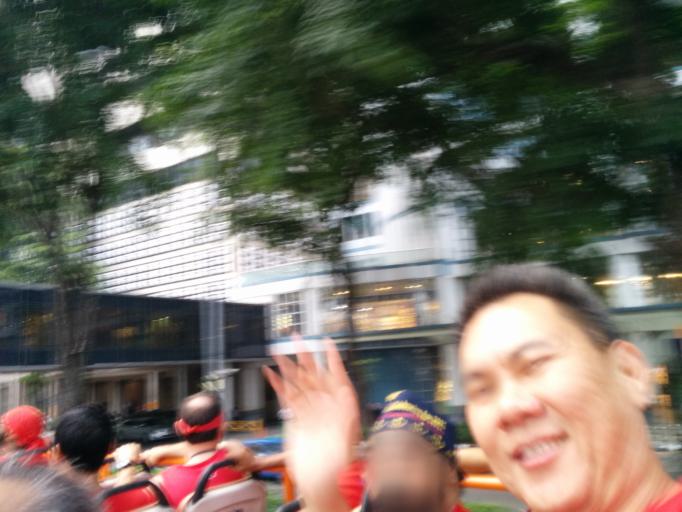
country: SG
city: Singapore
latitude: 1.2841
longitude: 103.8530
